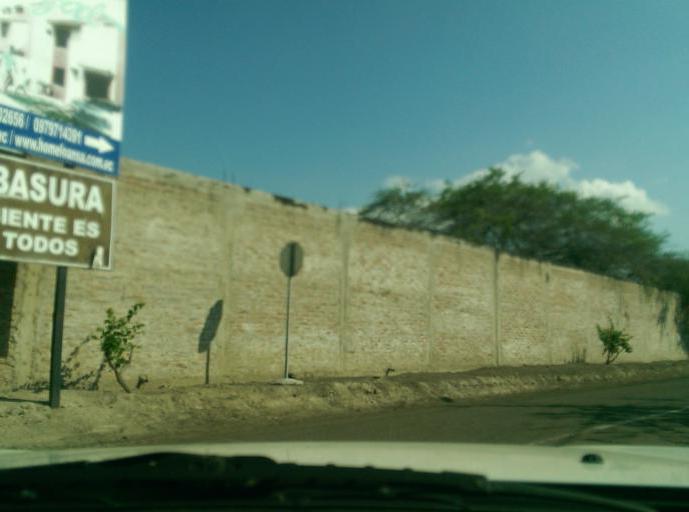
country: EC
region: Manabi
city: Manta
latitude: -0.9694
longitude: -80.7585
